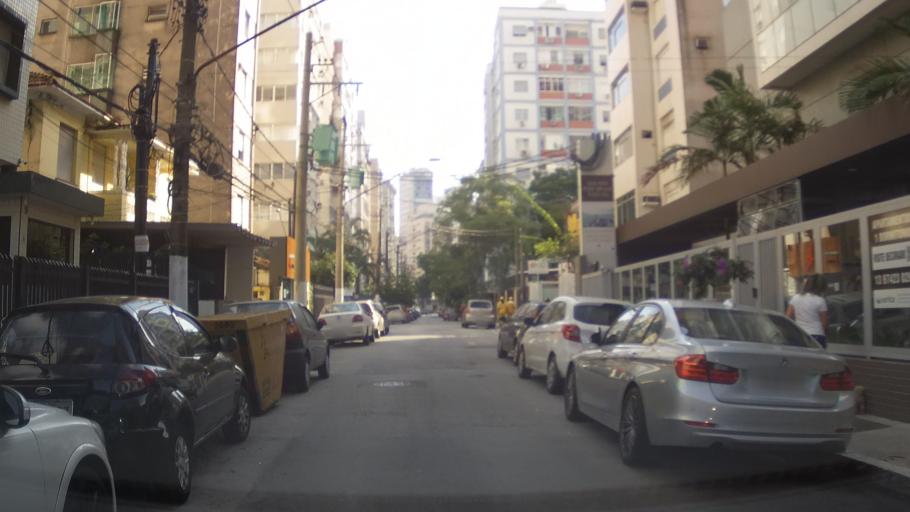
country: BR
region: Sao Paulo
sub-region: Santos
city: Santos
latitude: -23.9704
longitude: -46.3278
